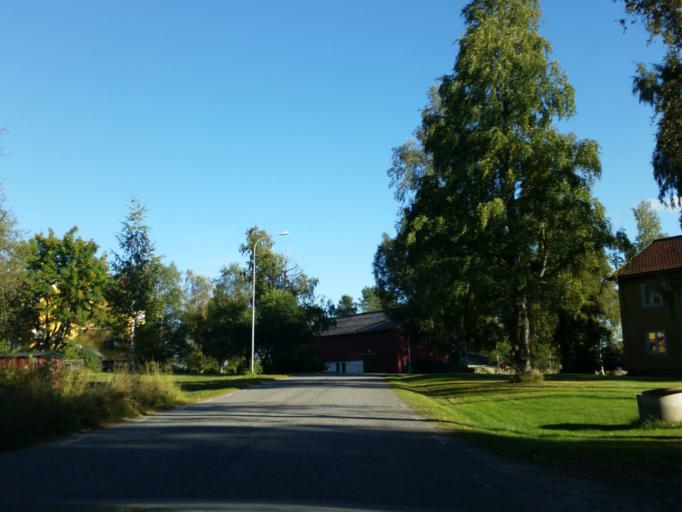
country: SE
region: Vaesterbotten
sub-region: Robertsfors Kommun
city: Robertsfors
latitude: 64.0452
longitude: 20.8577
